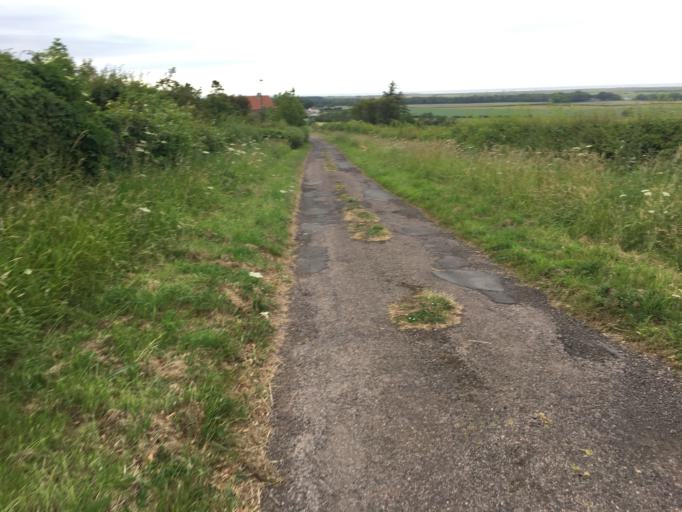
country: GB
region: England
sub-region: Northumberland
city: Lowick
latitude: 55.6652
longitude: -1.9142
